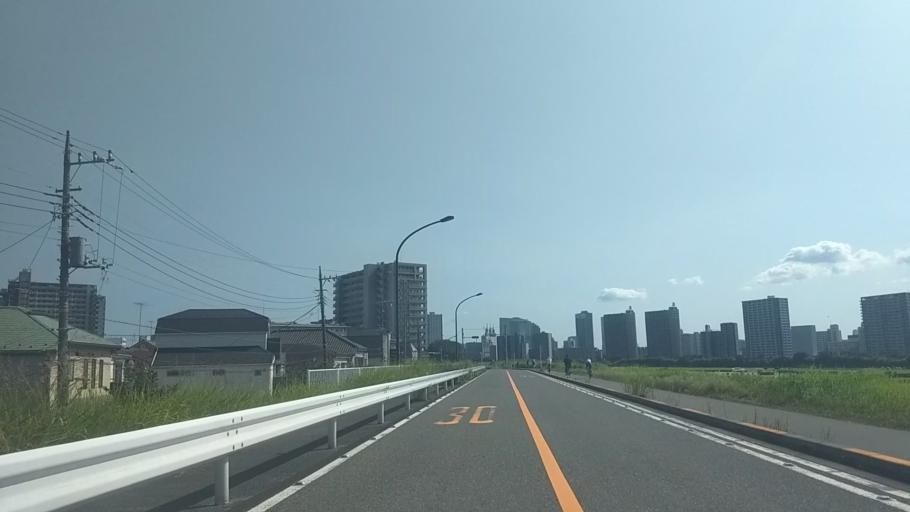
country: JP
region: Kanagawa
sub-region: Kawasaki-shi
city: Kawasaki
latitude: 35.5476
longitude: 139.7038
